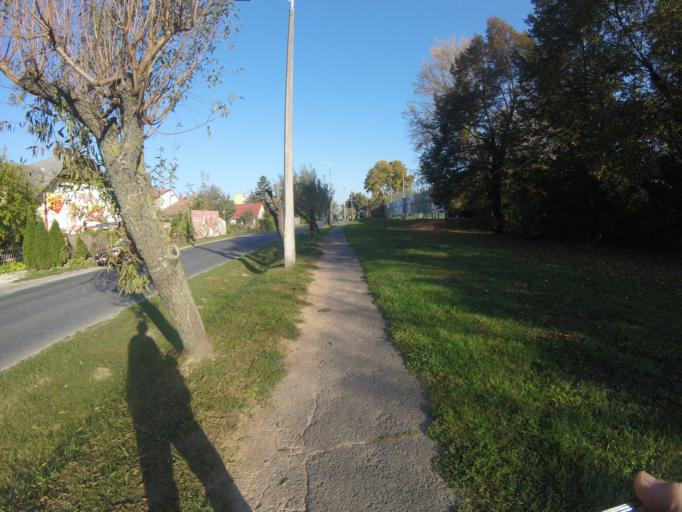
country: HU
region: Zala
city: Keszthely
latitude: 46.7648
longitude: 17.2499
